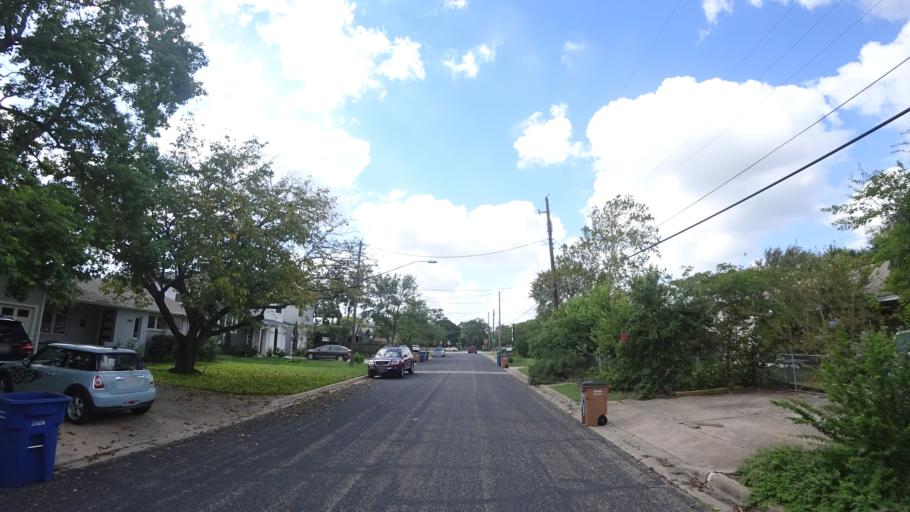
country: US
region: Texas
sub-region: Travis County
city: Austin
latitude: 30.3516
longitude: -97.7187
